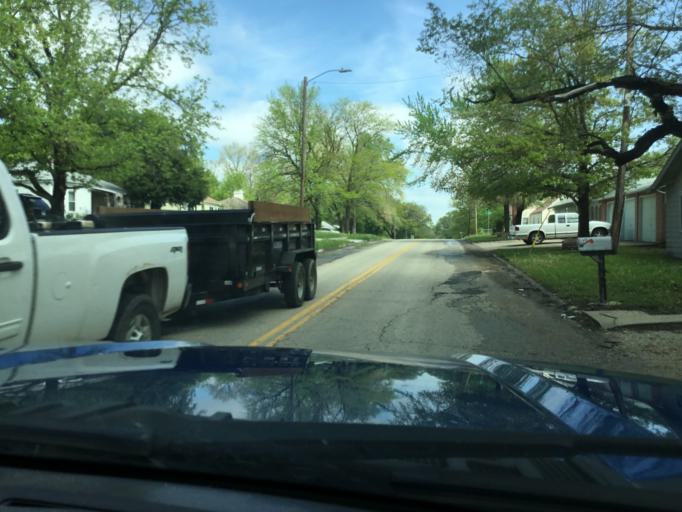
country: US
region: Kansas
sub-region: Shawnee County
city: Topeka
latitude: 39.0246
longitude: -95.6607
